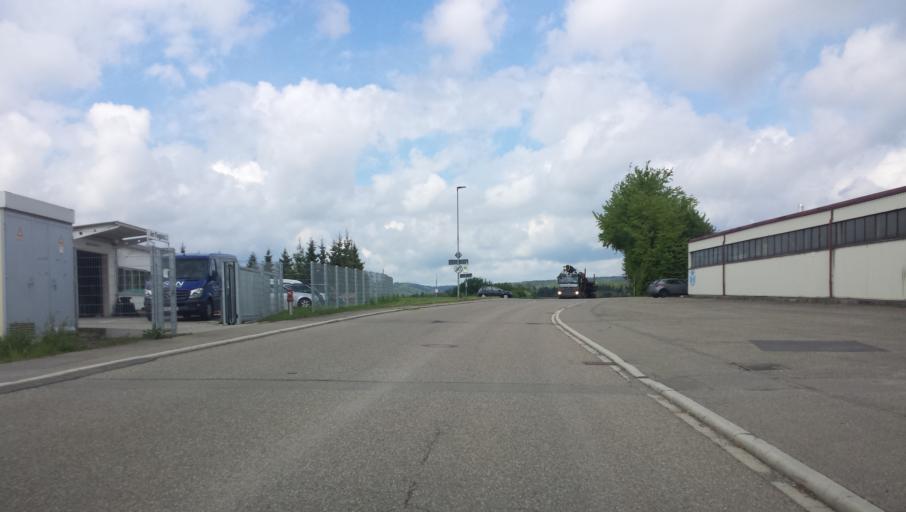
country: DE
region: Baden-Wuerttemberg
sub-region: Karlsruhe Region
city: Fahrenbach
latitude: 49.3991
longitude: 9.1220
